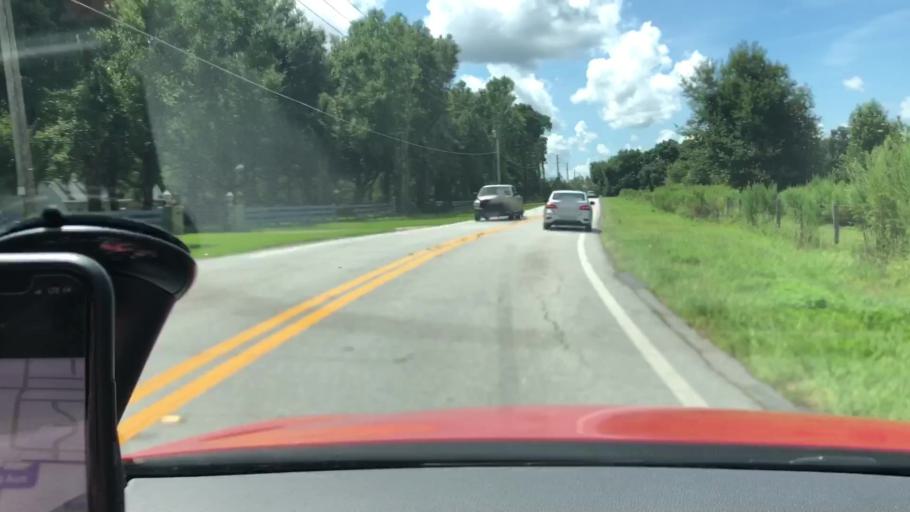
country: US
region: Florida
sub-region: Lake County
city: Eustis
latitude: 28.8379
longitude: -81.6545
